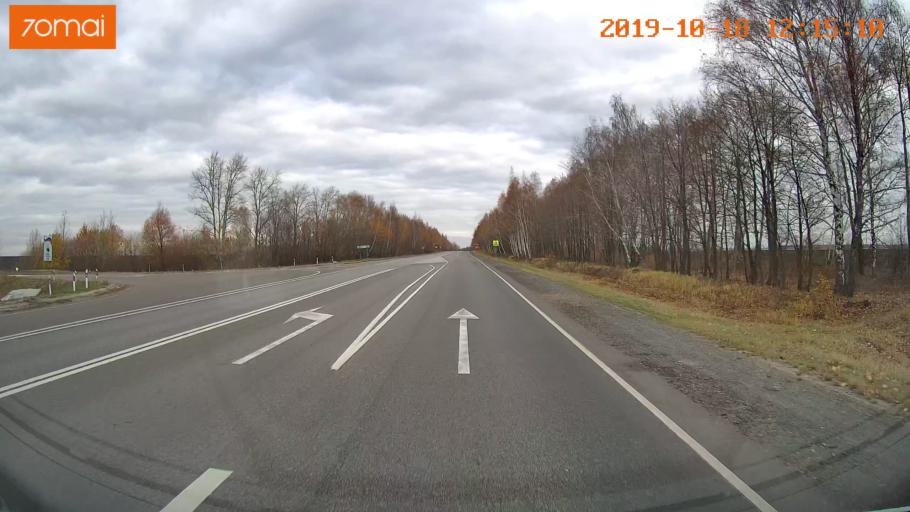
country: RU
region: Rjazan
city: Zakharovo
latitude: 54.4399
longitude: 39.3954
